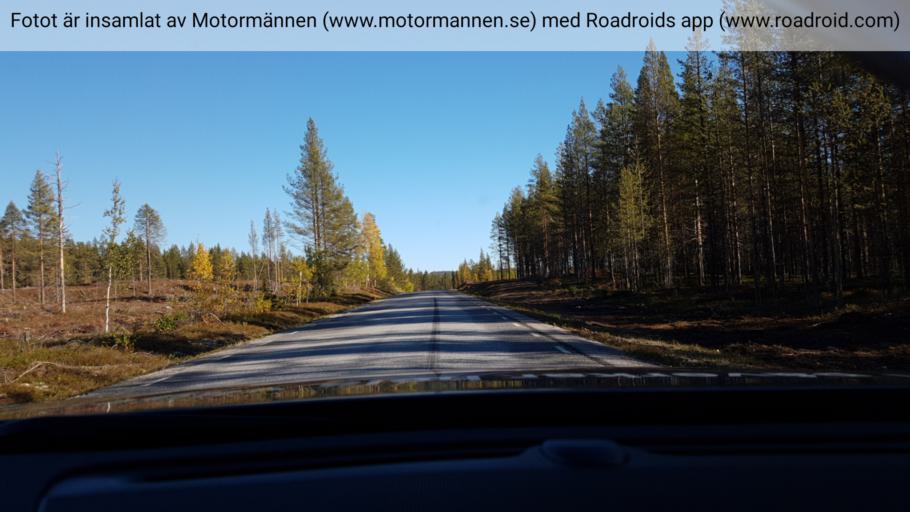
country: SE
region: Norrbotten
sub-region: Gallivare Kommun
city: Gaellivare
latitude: 66.4720
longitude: 20.8506
